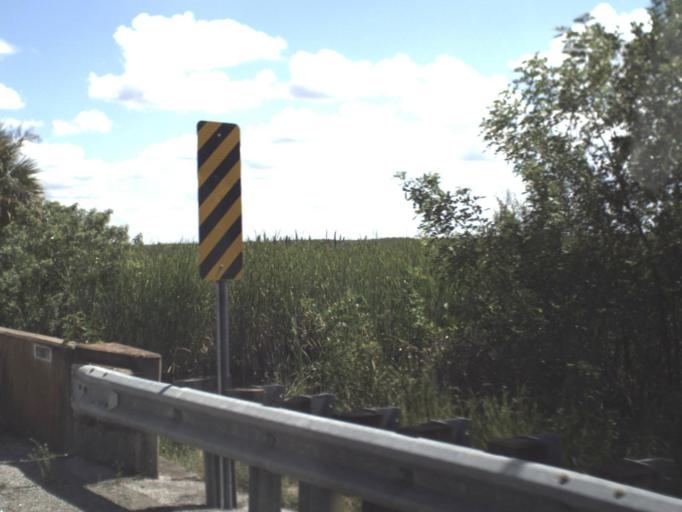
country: US
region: Florida
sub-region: Collier County
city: Marco
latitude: 25.9220
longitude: -81.4108
